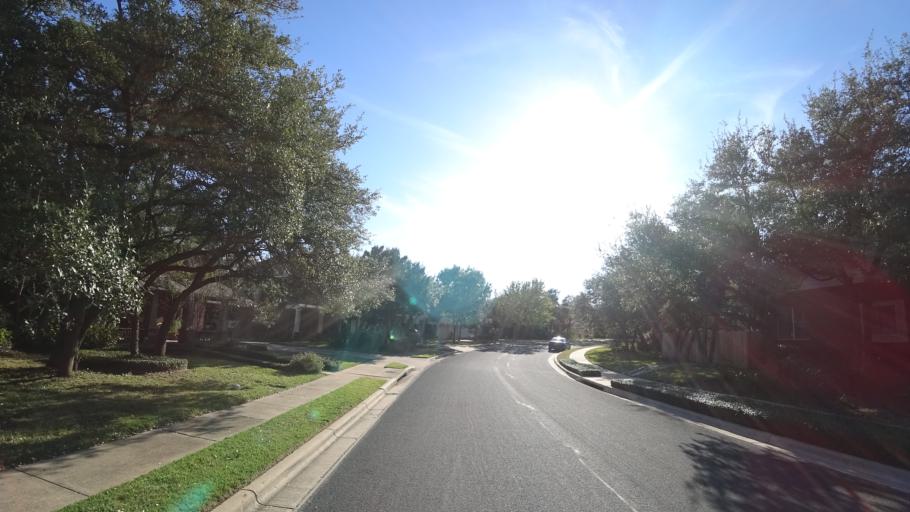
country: US
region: Texas
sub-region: Travis County
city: Barton Creek
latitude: 30.2511
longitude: -97.8422
